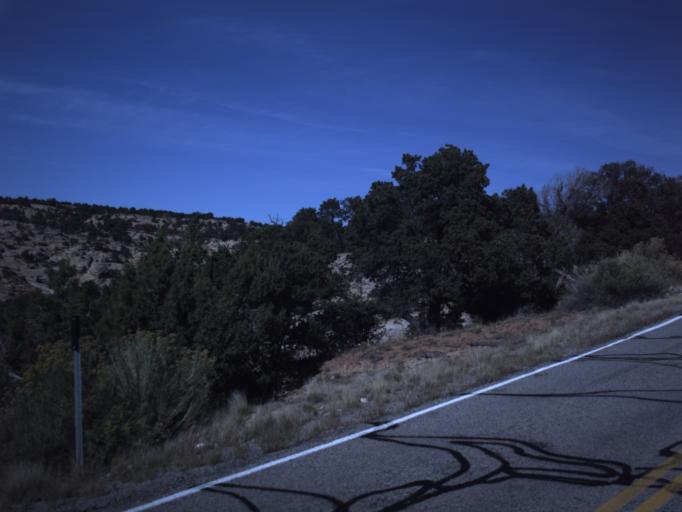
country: US
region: Utah
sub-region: San Juan County
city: Monticello
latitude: 37.9912
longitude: -109.4910
